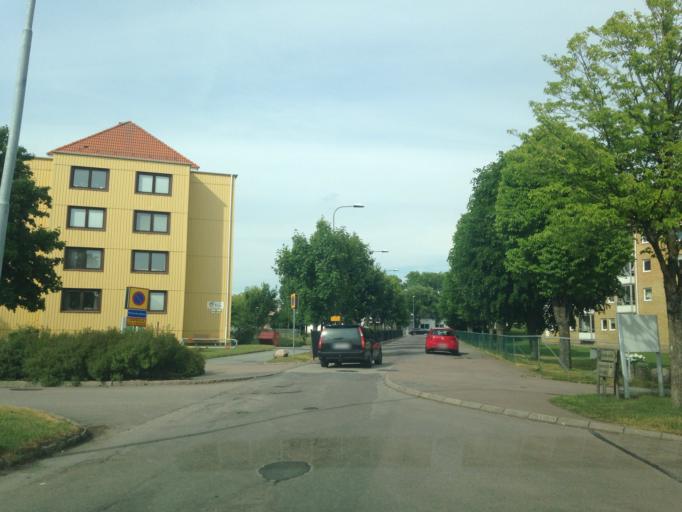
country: SE
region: Vaestra Goetaland
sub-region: Goteborg
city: Majorna
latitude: 57.7528
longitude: 11.9225
